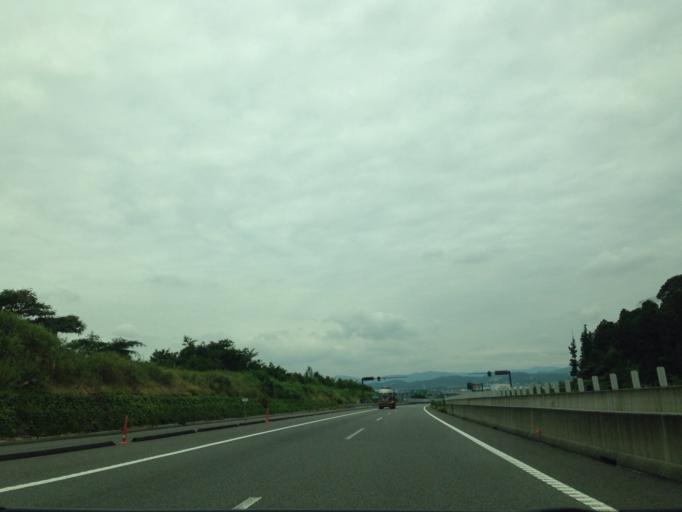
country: JP
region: Shizuoka
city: Hamakita
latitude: 34.8263
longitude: 137.8507
